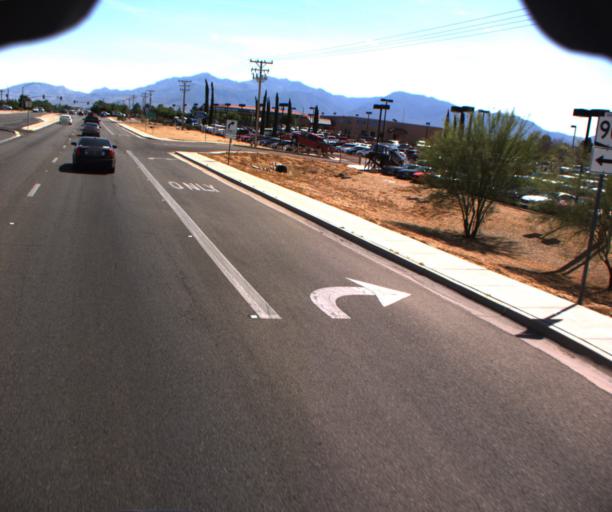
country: US
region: Arizona
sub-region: Cochise County
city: Sierra Vista
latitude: 31.5572
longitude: -110.2574
